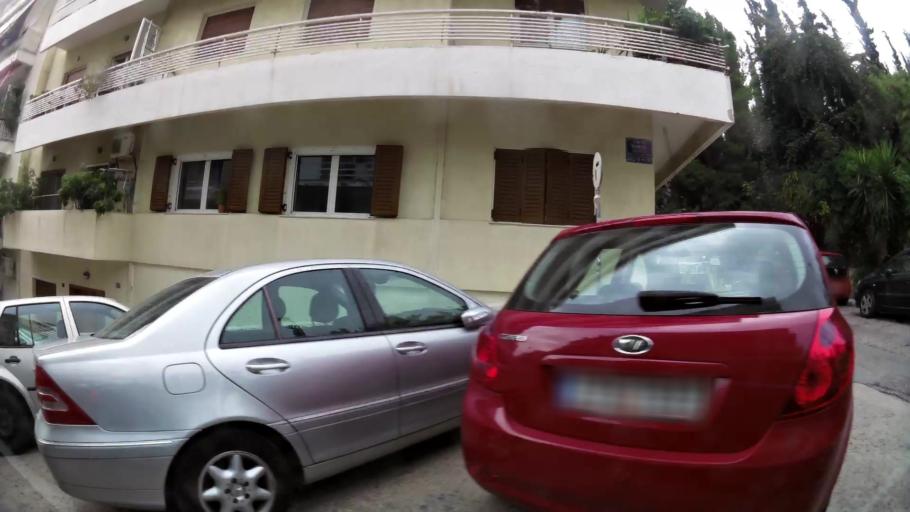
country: GR
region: Attica
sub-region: Nomarchia Athinas
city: Vyronas
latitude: 37.9741
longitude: 23.7544
